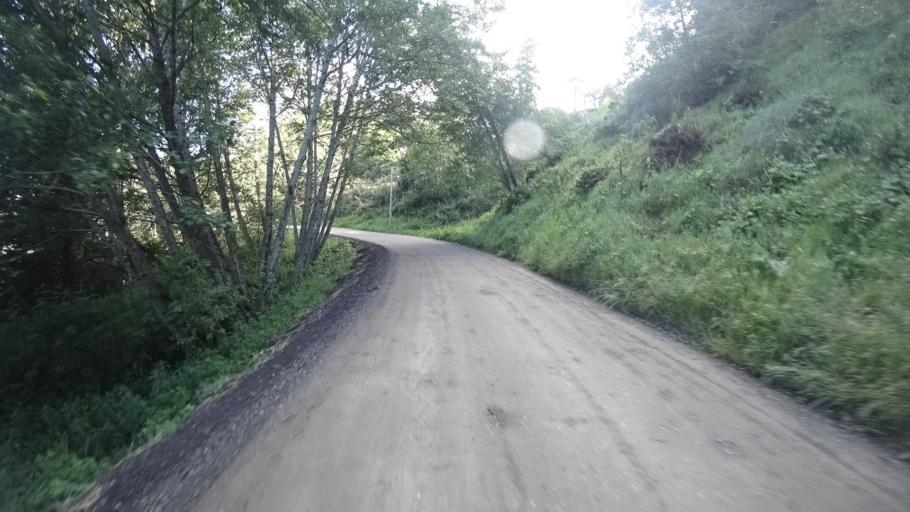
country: US
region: California
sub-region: Humboldt County
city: Westhaven-Moonstone
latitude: 41.0505
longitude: -124.1262
